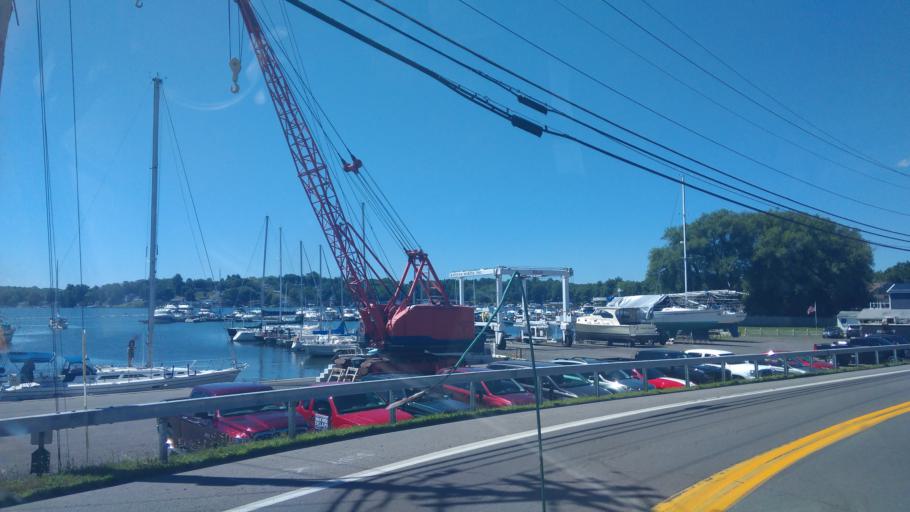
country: US
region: New York
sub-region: Wayne County
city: Sodus
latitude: 43.2683
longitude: -76.9891
